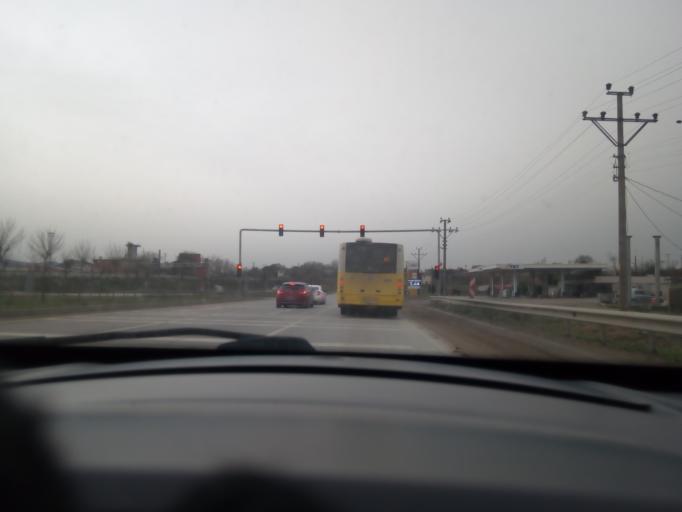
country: TR
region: Balikesir
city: Susurluk
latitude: 39.9528
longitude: 28.1705
